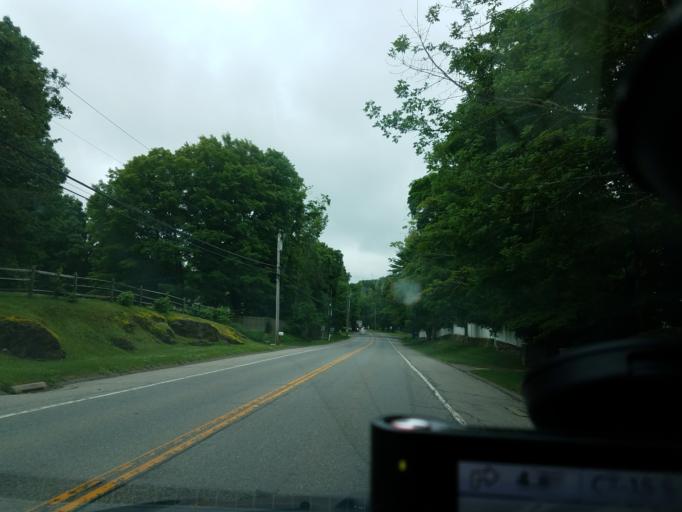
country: US
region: Connecticut
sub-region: Fairfield County
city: New Canaan
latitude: 41.1867
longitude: -73.5048
